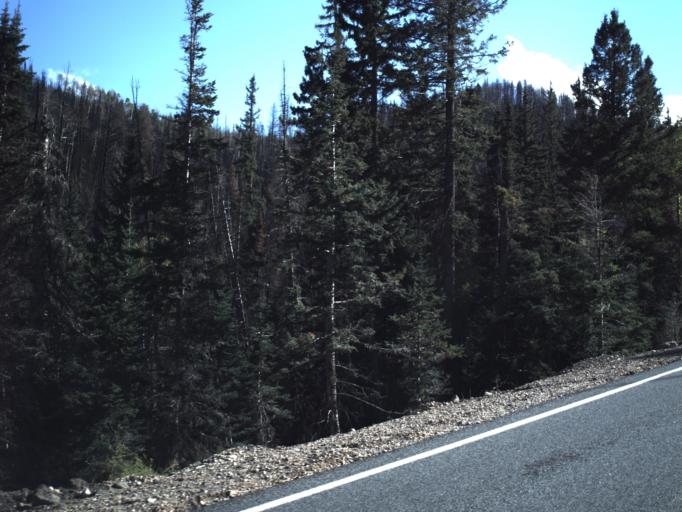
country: US
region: Utah
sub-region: Iron County
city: Parowan
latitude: 37.7233
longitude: -112.8427
